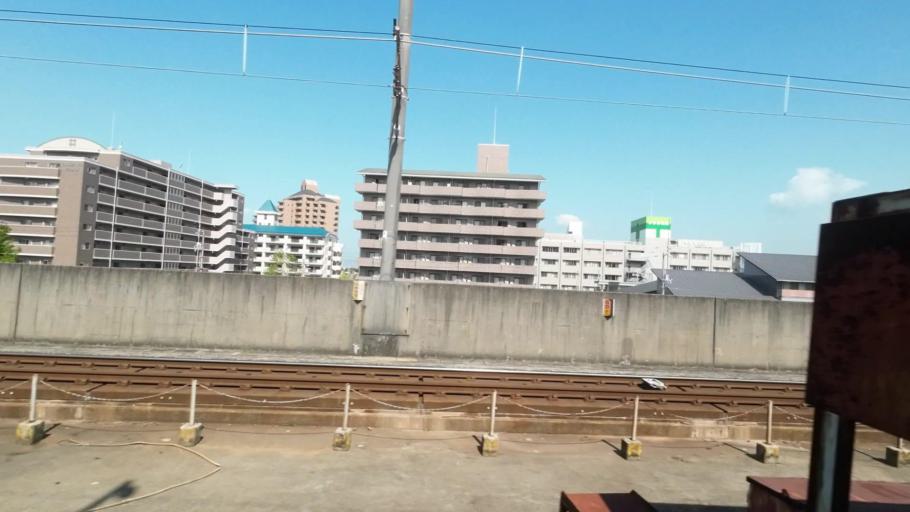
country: JP
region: Kagawa
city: Sakaidecho
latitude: 34.3031
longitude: 133.8119
